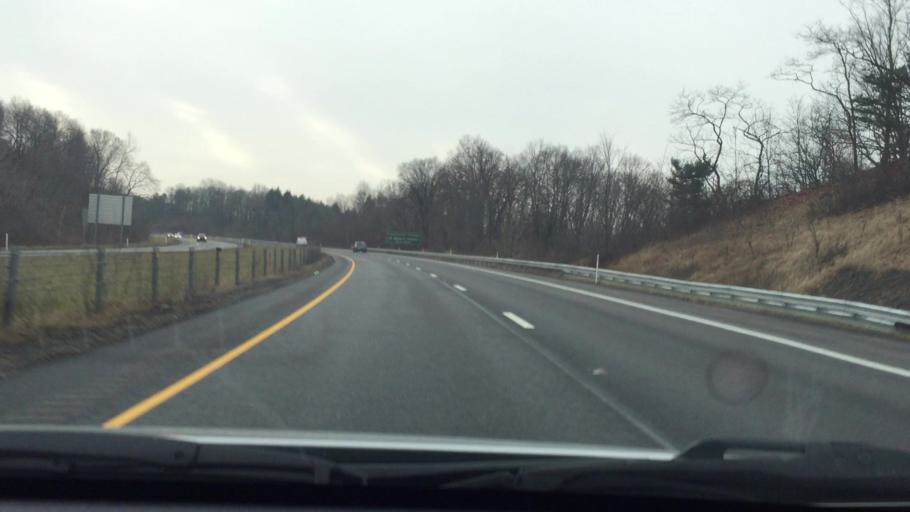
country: US
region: Pennsylvania
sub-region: Beaver County
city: Beaver
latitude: 40.6527
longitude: -80.3252
